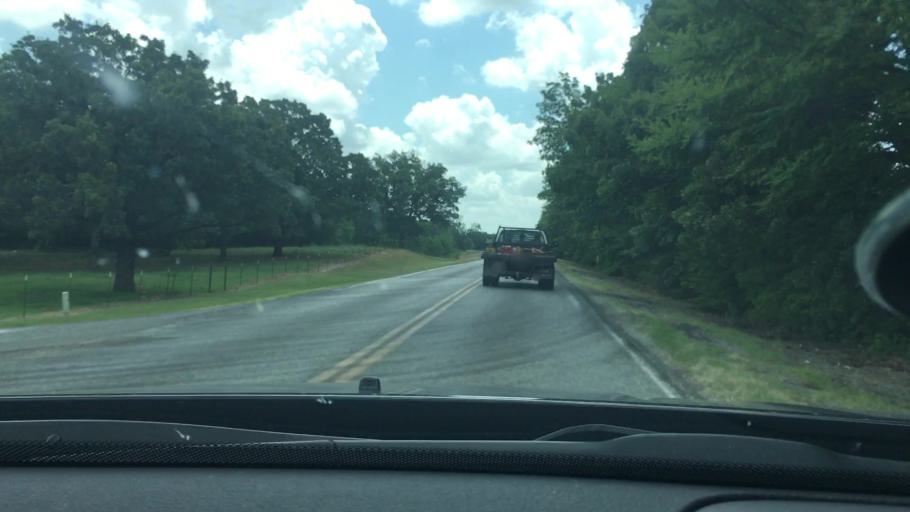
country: US
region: Oklahoma
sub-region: Pontotoc County
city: Ada
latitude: 34.5783
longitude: -96.6328
